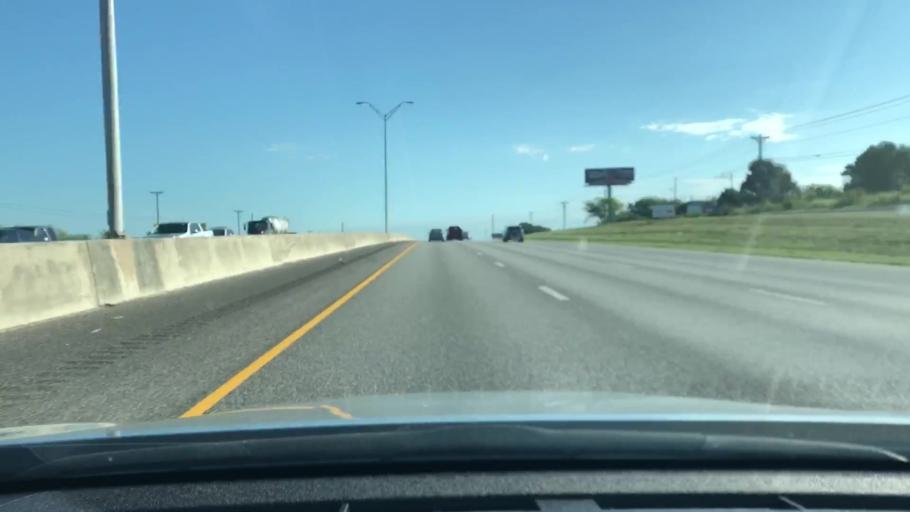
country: US
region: Texas
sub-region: Guadalupe County
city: Northcliff
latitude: 29.6432
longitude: -98.2057
